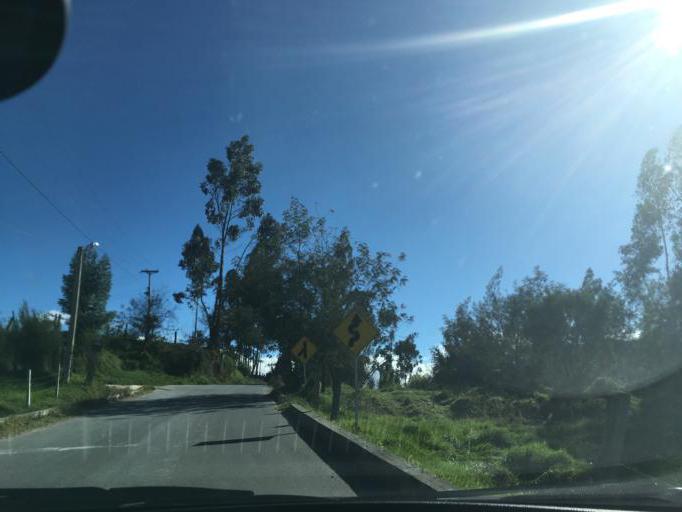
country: CO
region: Boyaca
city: Firavitoba
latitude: 5.6016
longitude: -72.9795
